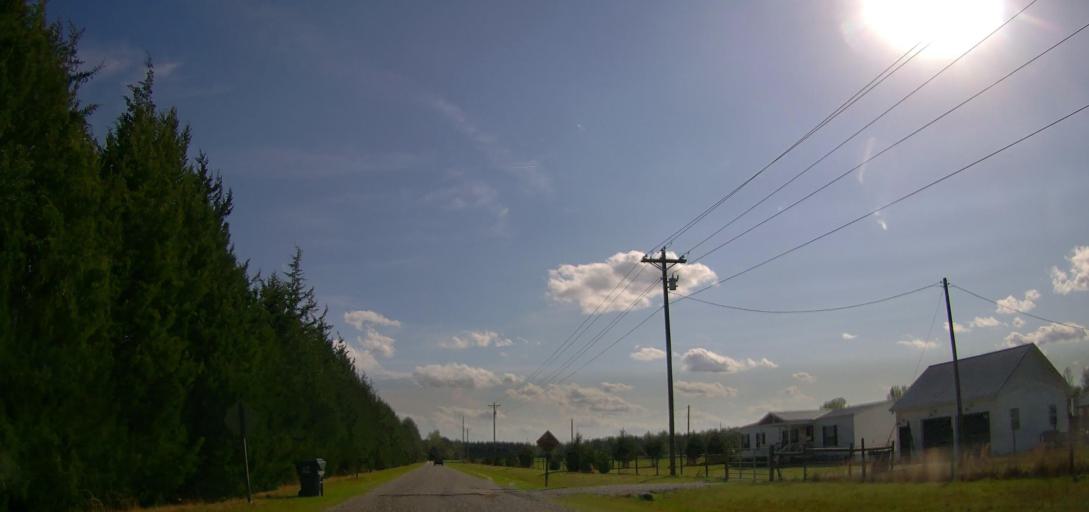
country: US
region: Georgia
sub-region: Baldwin County
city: Hardwick
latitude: 33.0251
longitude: -83.1182
